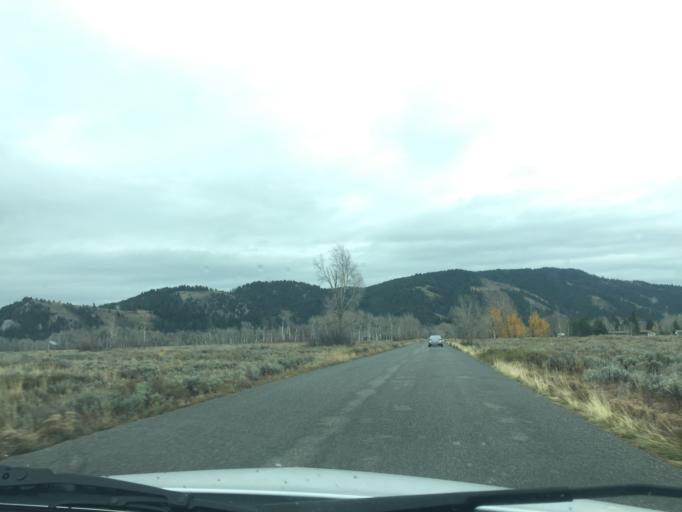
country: US
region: Wyoming
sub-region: Teton County
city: Moose Wilson Road
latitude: 43.6626
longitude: -110.7196
